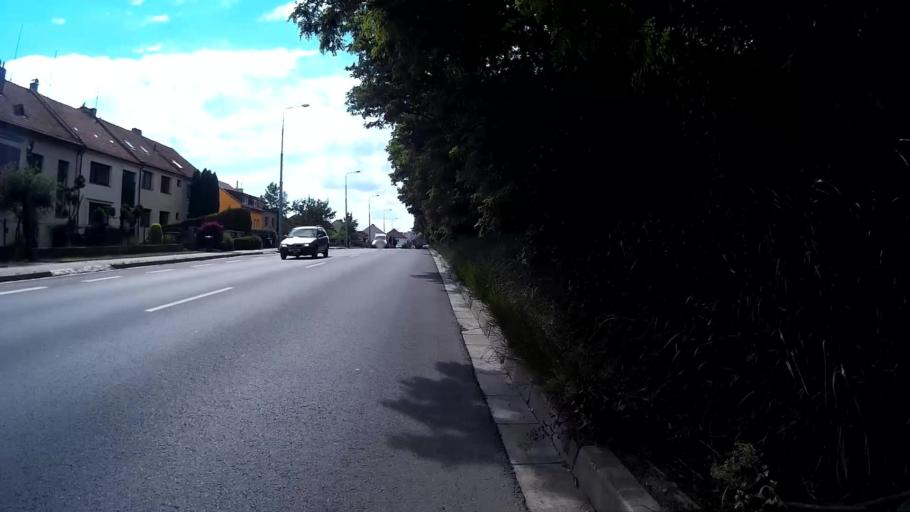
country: CZ
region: South Moravian
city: Moravany
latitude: 49.1645
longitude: 16.5909
